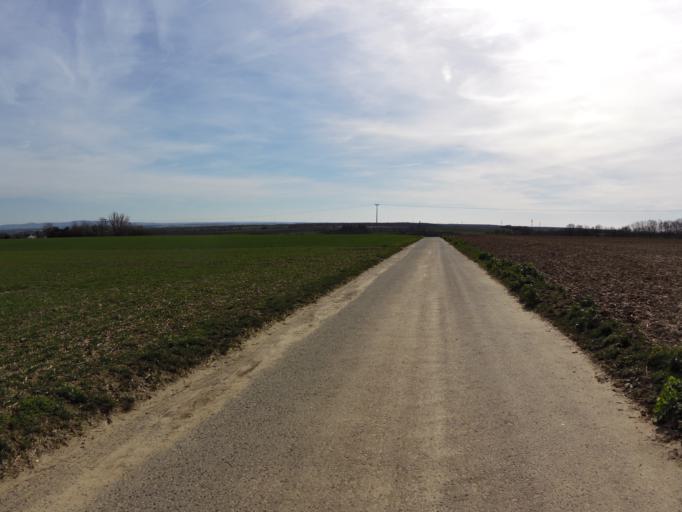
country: DE
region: Bavaria
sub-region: Regierungsbezirk Unterfranken
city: Buchbrunn
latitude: 49.7563
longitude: 10.1124
